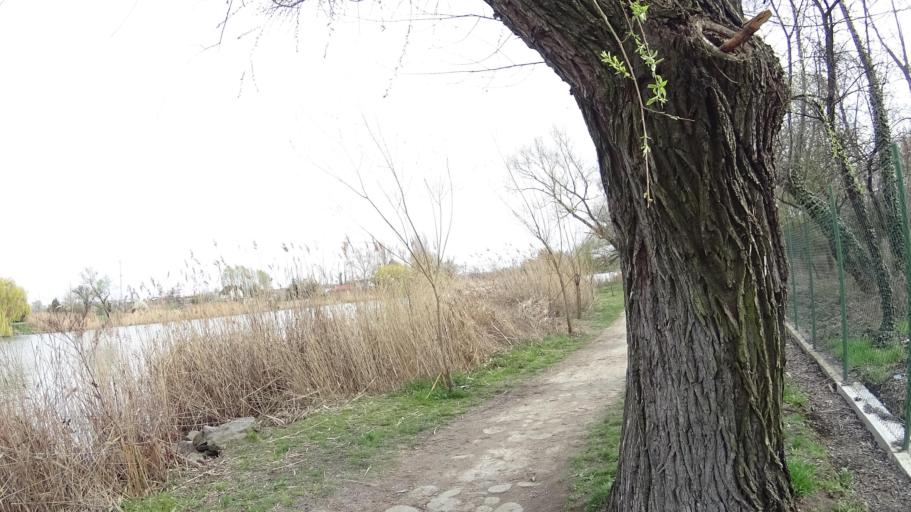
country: HU
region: Budapest
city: Budapest XX. keruelet
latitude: 47.4148
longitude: 19.0981
